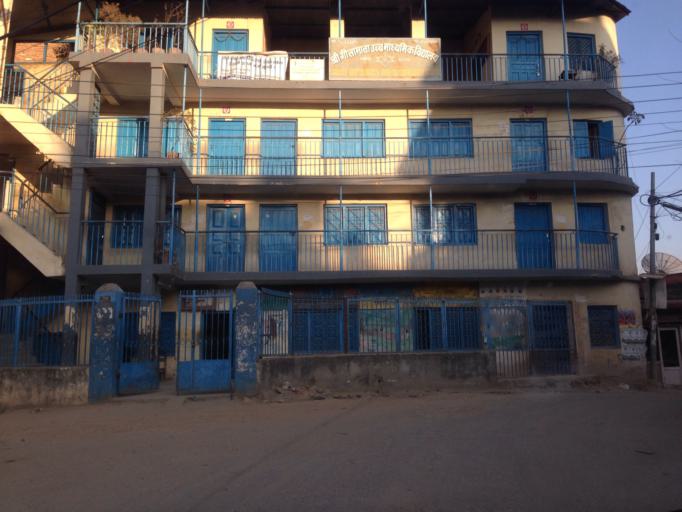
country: NP
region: Central Region
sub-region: Bagmati Zone
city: Kathmandu
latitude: 27.7137
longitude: 85.2996
